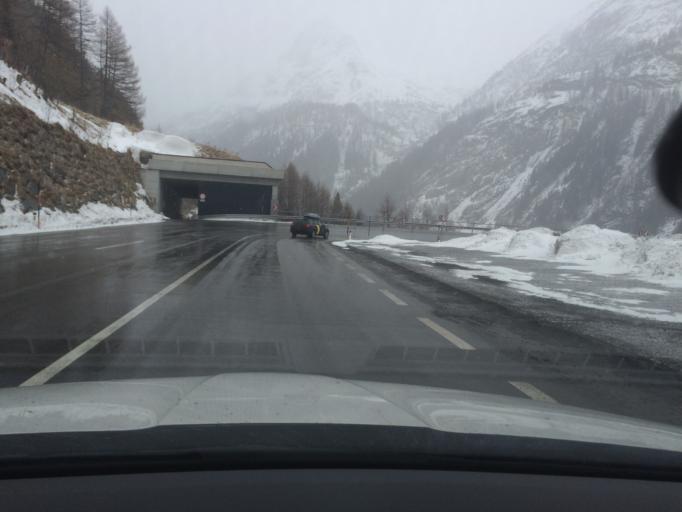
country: AT
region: Tyrol
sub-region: Politischer Bezirk Lienz
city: Matrei in Osttirol
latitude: 47.1161
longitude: 12.5062
